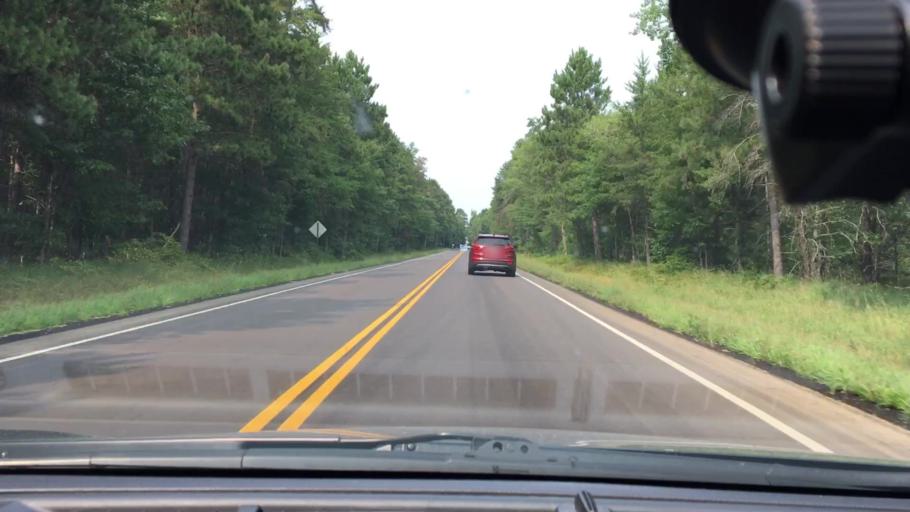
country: US
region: Minnesota
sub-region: Crow Wing County
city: Breezy Point
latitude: 46.5303
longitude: -94.1822
